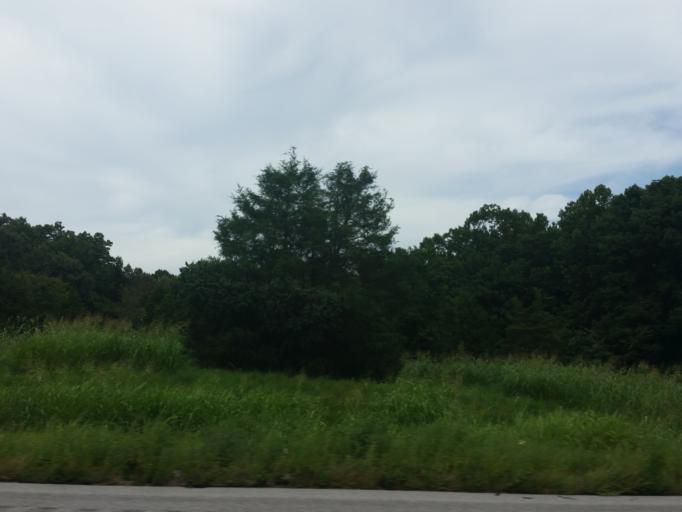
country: US
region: Kentucky
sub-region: Trigg County
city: Cadiz
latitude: 36.9484
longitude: -87.8416
